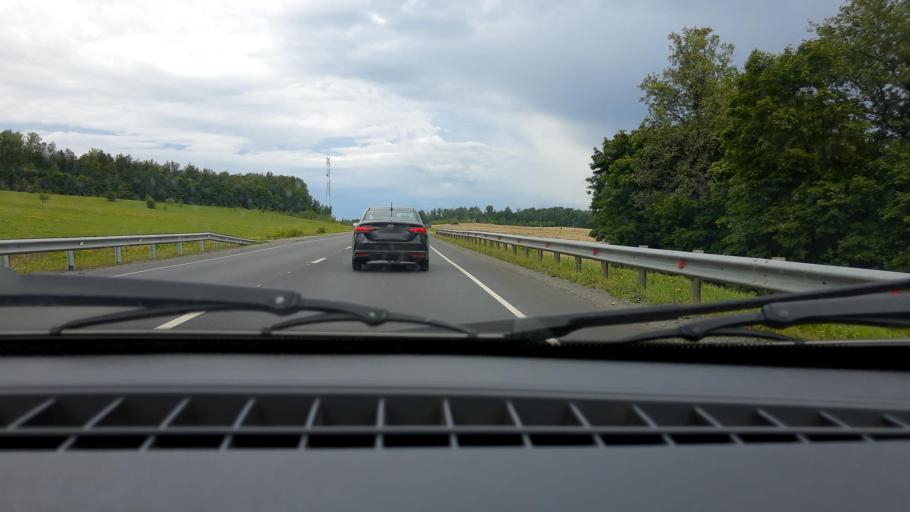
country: RU
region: Bashkortostan
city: Avdon
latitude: 54.8267
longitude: 55.7266
